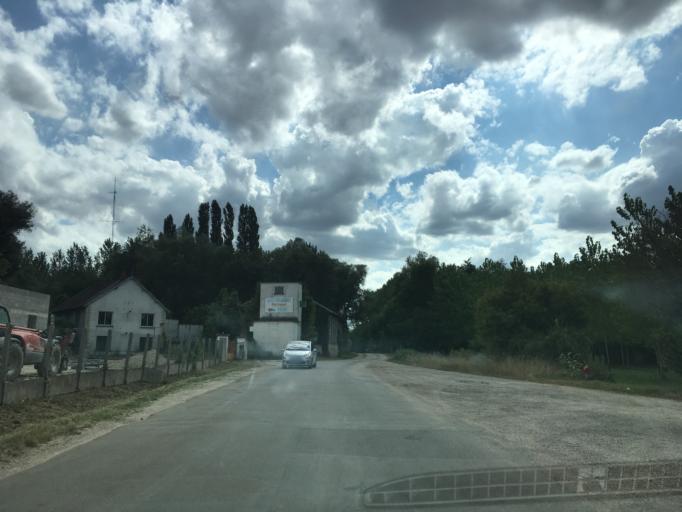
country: FR
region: Bourgogne
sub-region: Departement de l'Yonne
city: Joigny
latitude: 47.9724
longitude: 3.3841
